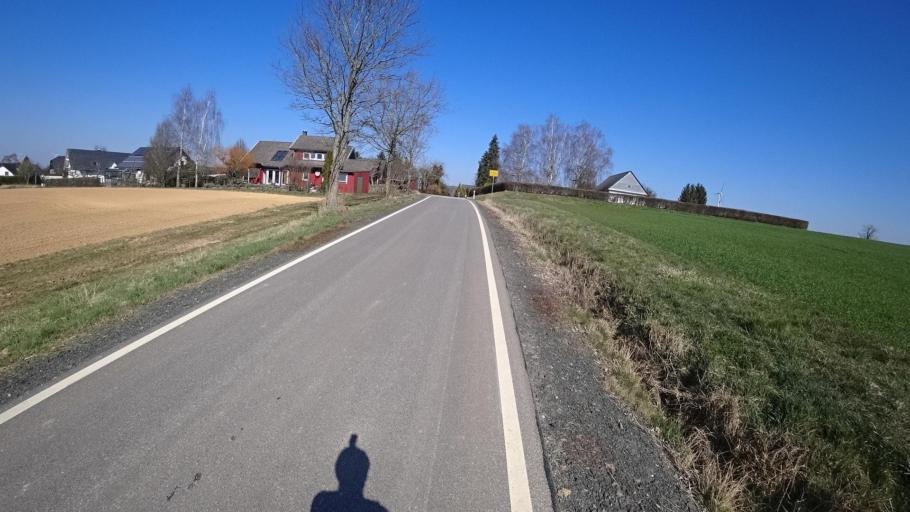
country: DE
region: Rheinland-Pfalz
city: Mutterschied
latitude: 49.9927
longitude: 7.5679
